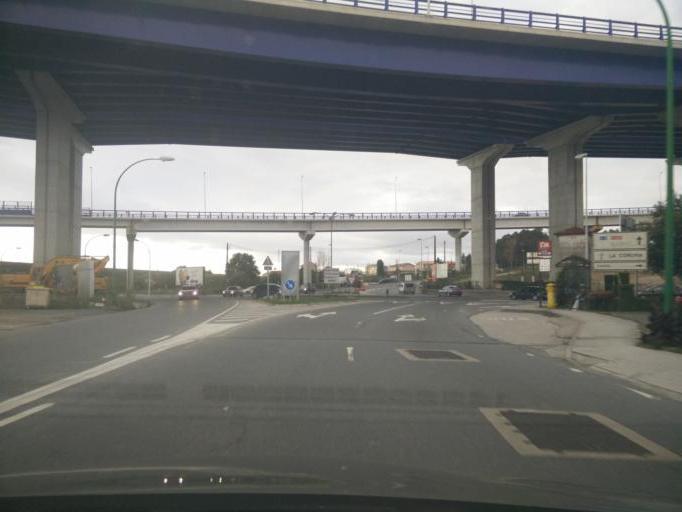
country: ES
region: Galicia
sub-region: Provincia da Coruna
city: A Coruna
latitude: 43.3364
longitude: -8.4226
